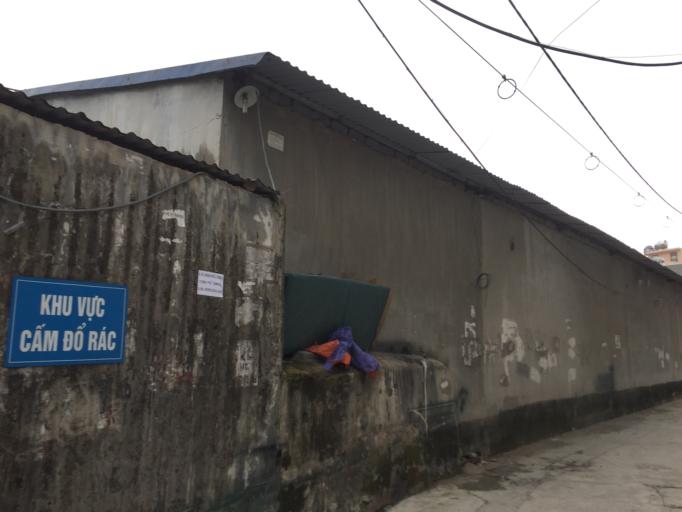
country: VN
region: Ha Noi
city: Thanh Xuan
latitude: 20.9895
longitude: 105.8091
